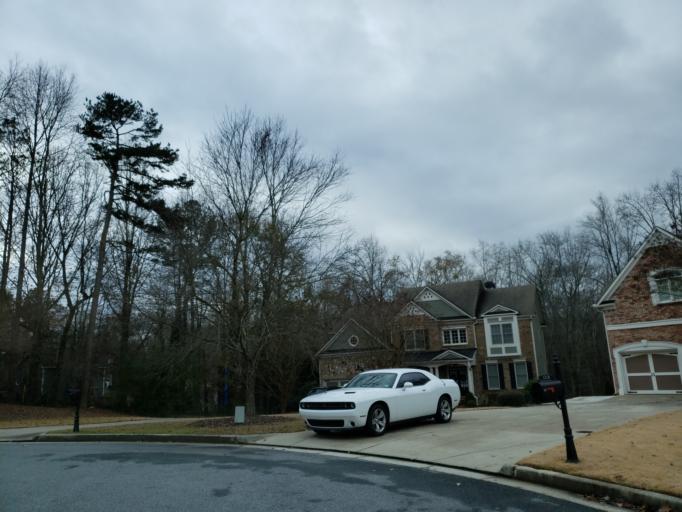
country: US
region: Georgia
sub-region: Cobb County
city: Fair Oaks
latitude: 33.9207
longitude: -84.6248
